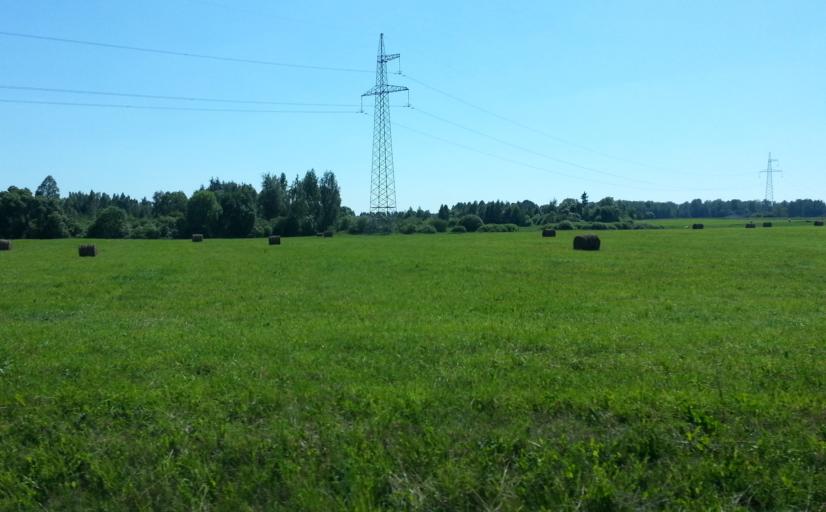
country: LT
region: Panevezys
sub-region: Birzai
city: Birzai
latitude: 56.2154
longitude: 24.6614
